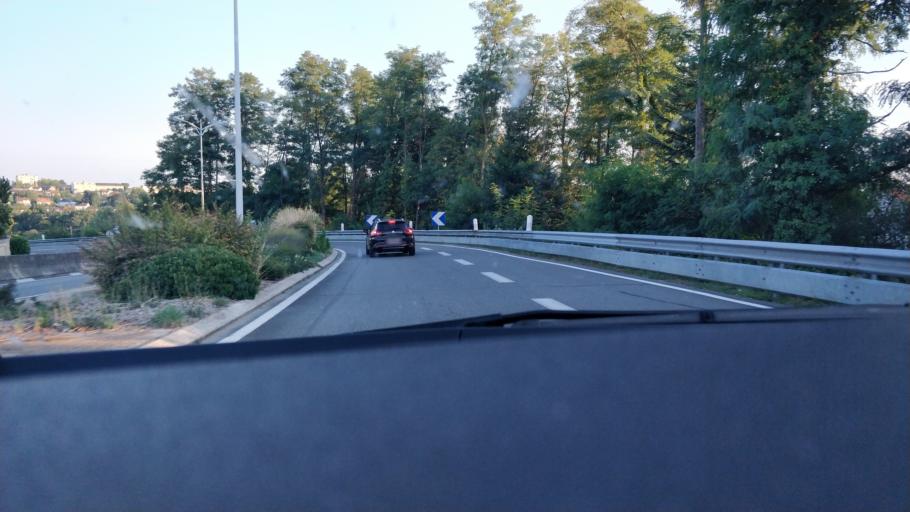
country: FR
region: Limousin
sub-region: Departement de la Haute-Vienne
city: Couzeix
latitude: 45.8595
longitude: 1.2399
